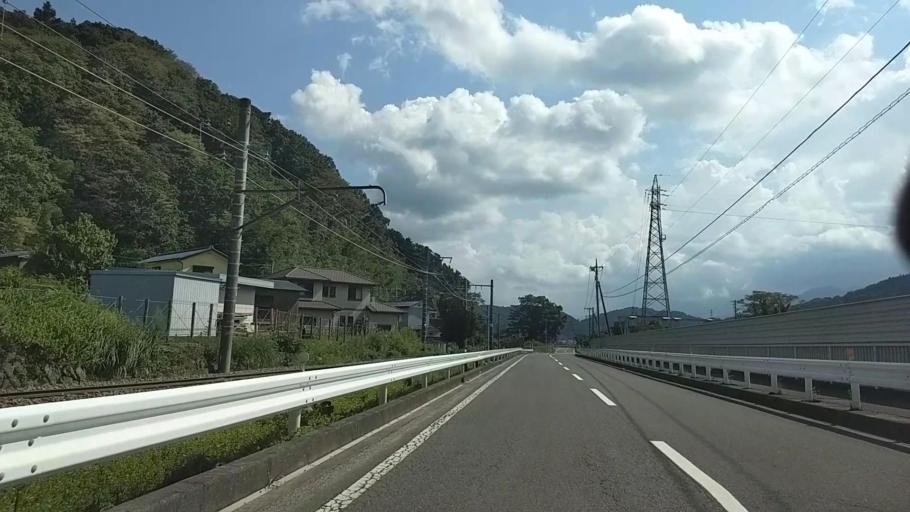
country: JP
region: Shizuoka
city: Fujinomiya
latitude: 35.3770
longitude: 138.4522
